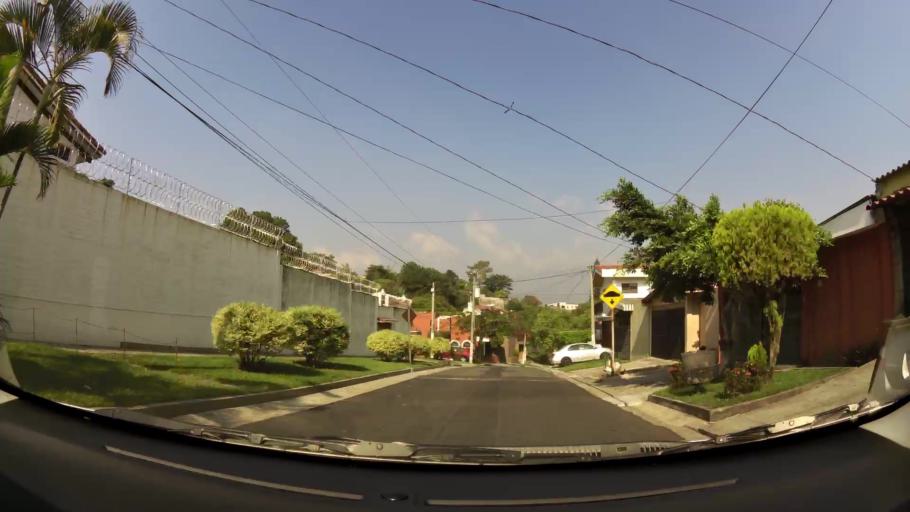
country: SV
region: La Libertad
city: Antiguo Cuscatlan
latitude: 13.6769
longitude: -89.2320
